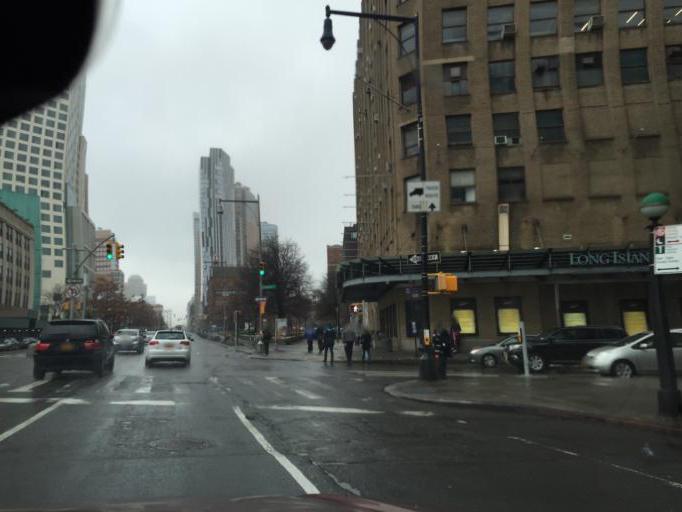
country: US
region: New York
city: New York City
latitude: 40.6898
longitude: -73.9813
